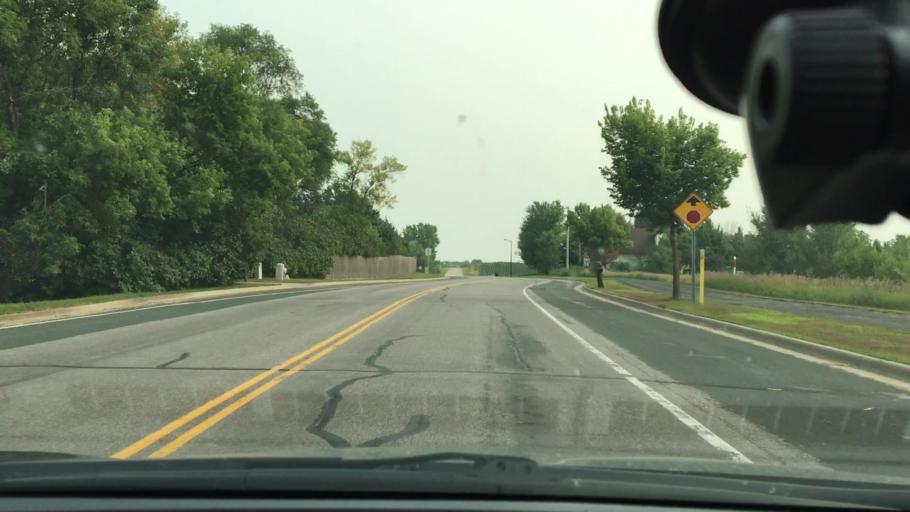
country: US
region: Minnesota
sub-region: Wright County
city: Otsego
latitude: 45.2544
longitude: -93.5913
